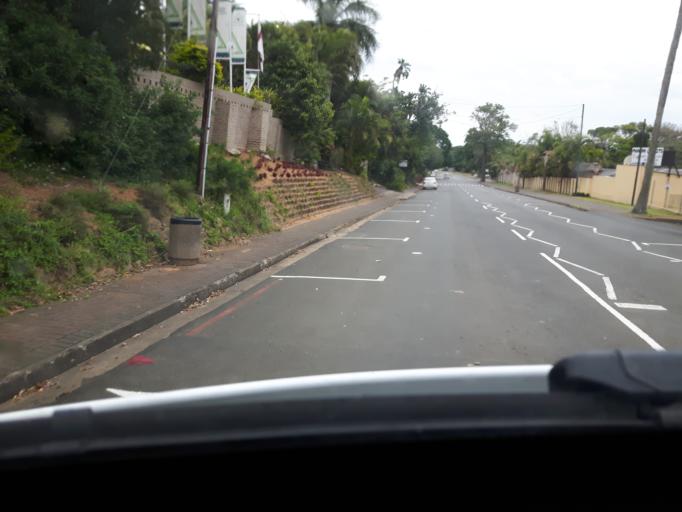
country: ZA
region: KwaZulu-Natal
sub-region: uMkhanyakude District Municipality
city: Mtubatuba
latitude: -28.3781
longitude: 32.4105
